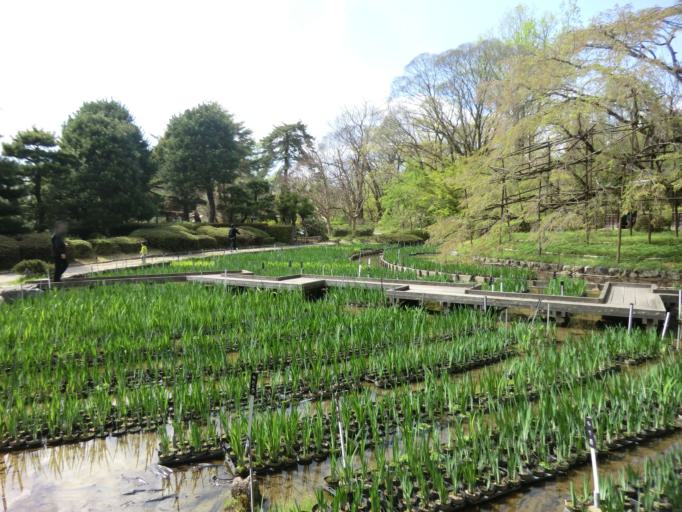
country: JP
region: Kyoto
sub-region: Kyoto-shi
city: Kamigyo-ku
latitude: 35.0488
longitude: 135.7641
